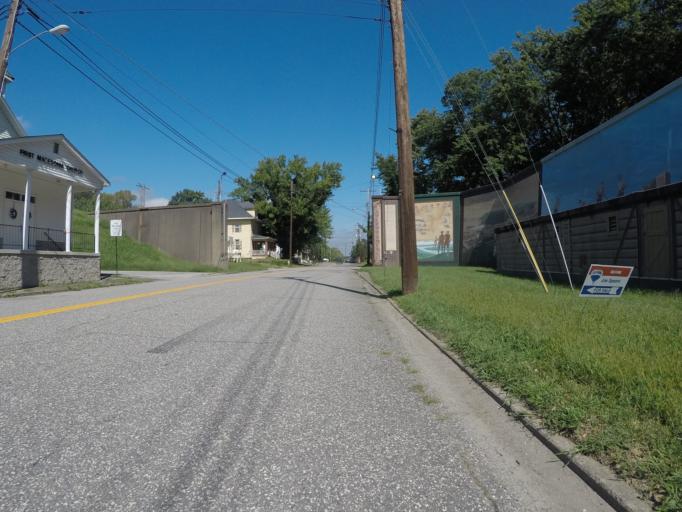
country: US
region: Ohio
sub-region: Lawrence County
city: South Point
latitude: 38.4230
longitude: -82.5998
